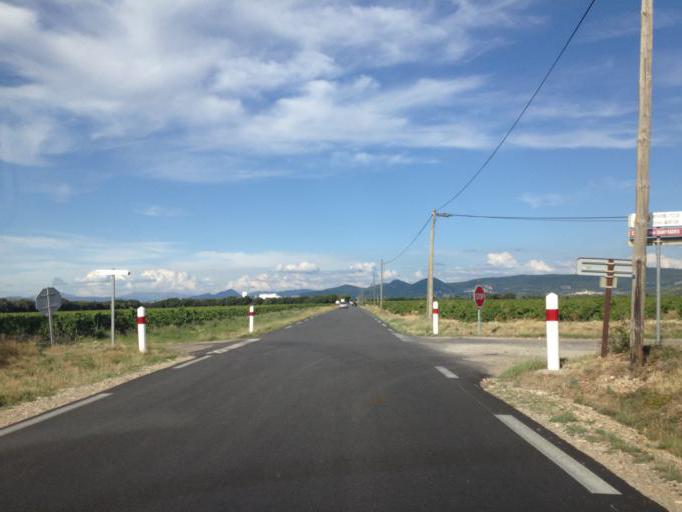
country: FR
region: Provence-Alpes-Cote d'Azur
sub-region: Departement du Vaucluse
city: Violes
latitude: 44.1797
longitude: 4.9446
